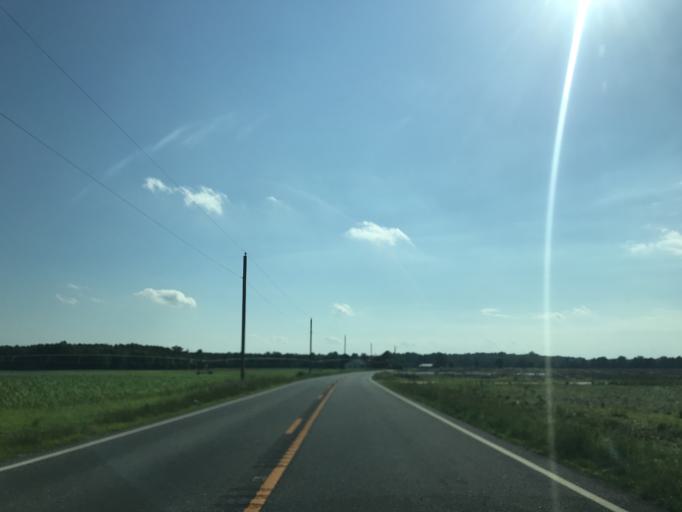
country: US
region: Maryland
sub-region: Wicomico County
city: Hebron
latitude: 38.4615
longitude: -75.6841
